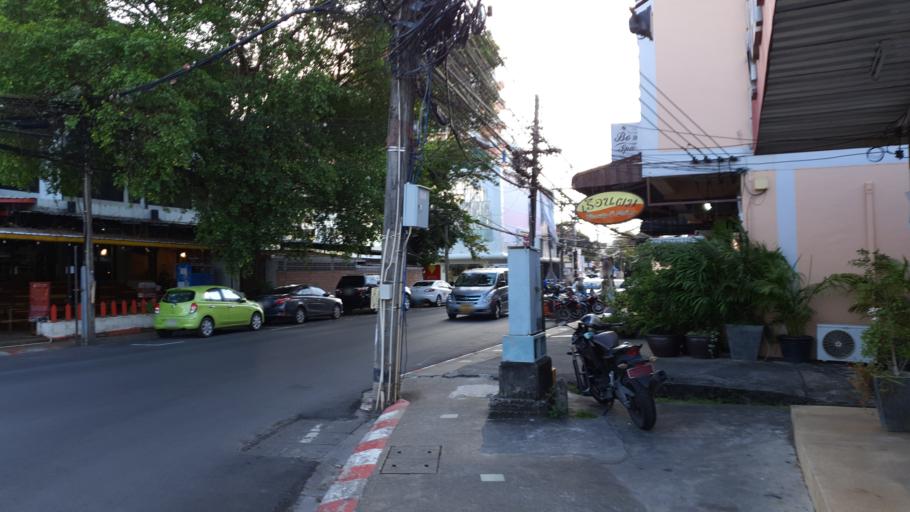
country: TH
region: Phuket
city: Ban Talat Nua
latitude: 7.8835
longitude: 98.3927
